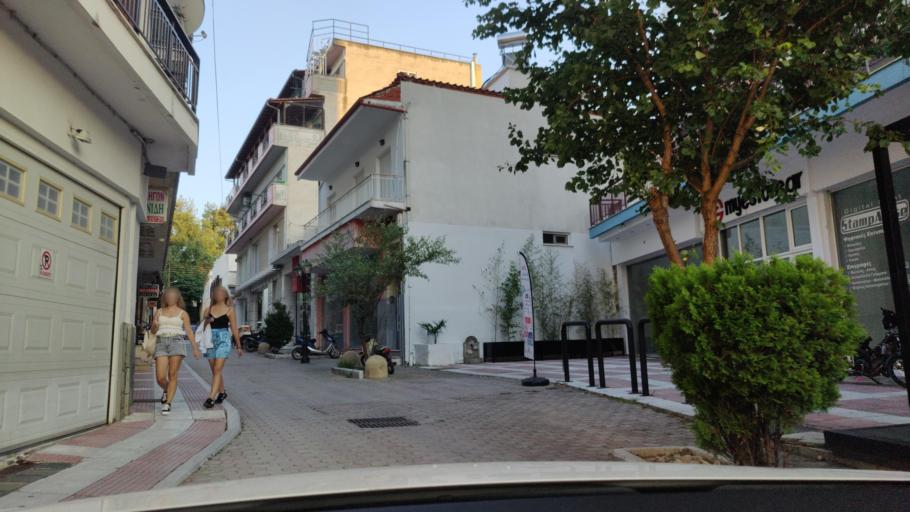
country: GR
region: Central Macedonia
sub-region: Nomos Serron
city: Sidirokastro
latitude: 41.2368
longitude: 23.3913
